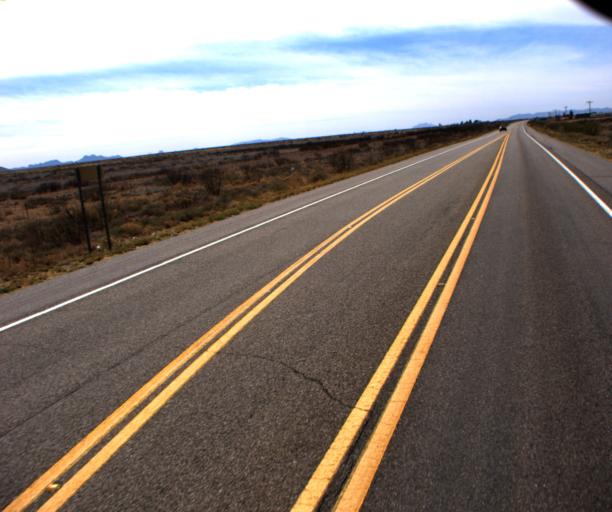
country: US
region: Arizona
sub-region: Cochise County
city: Pirtleville
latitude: 31.5971
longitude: -109.6699
